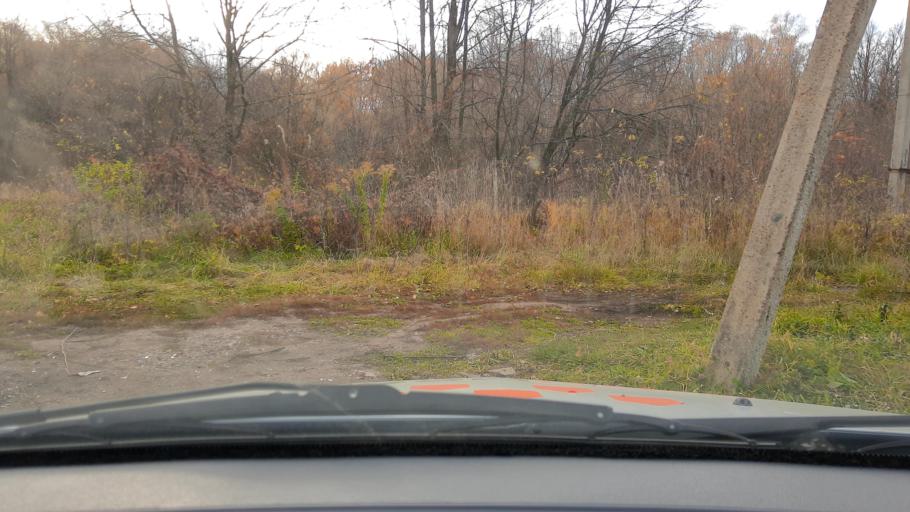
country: RU
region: Bashkortostan
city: Asanovo
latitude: 54.8020
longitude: 55.6135
